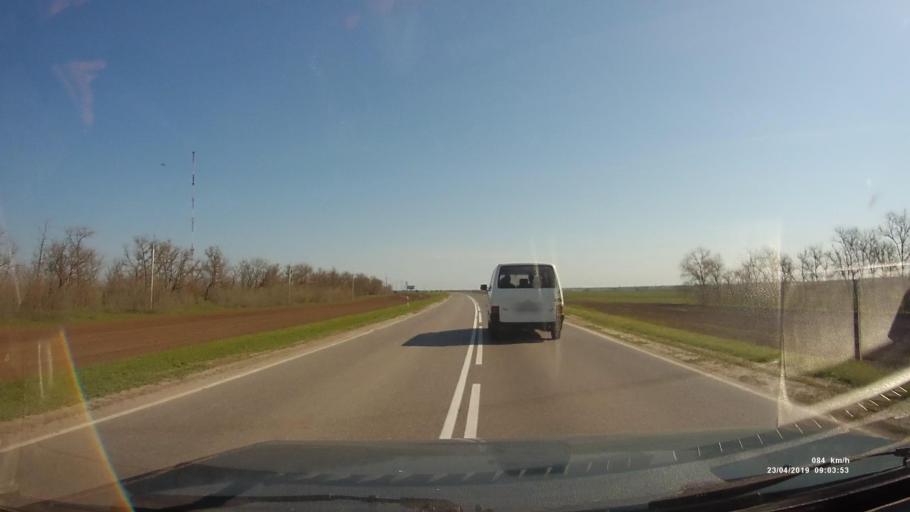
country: RU
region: Rostov
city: Sal'sk
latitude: 46.5268
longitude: 41.5758
